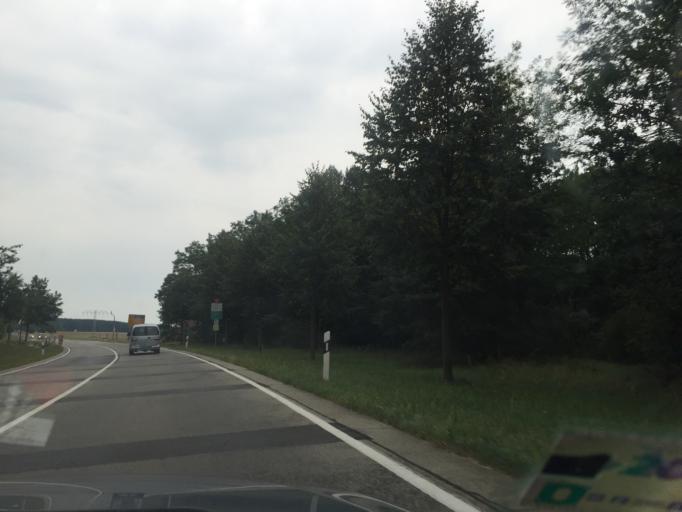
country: DE
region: Brandenburg
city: Wandlitz
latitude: 52.7470
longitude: 13.4306
